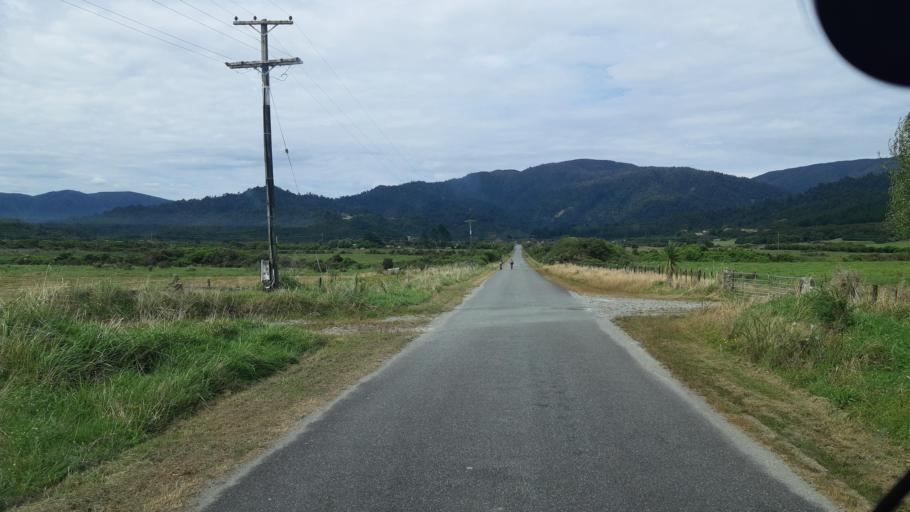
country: NZ
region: West Coast
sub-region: Westland District
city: Hokitika
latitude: -42.8858
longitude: 170.8042
